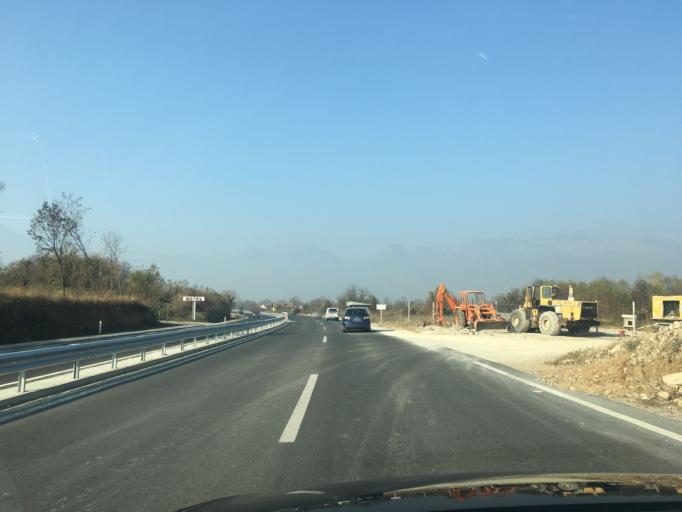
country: XK
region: Pec
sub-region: Komuna e Pejes
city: Dubova (Driloni)
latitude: 42.6579
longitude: 20.3849
